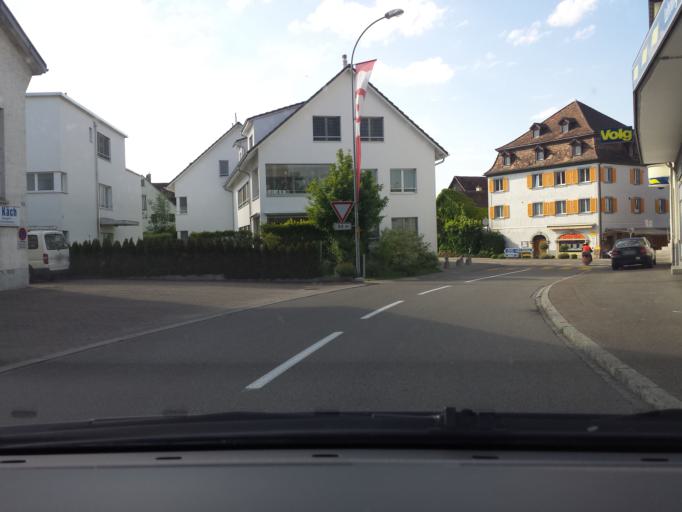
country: CH
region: Saint Gallen
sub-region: Wahlkreis Rorschach
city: Horn
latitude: 47.4954
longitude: 9.4629
